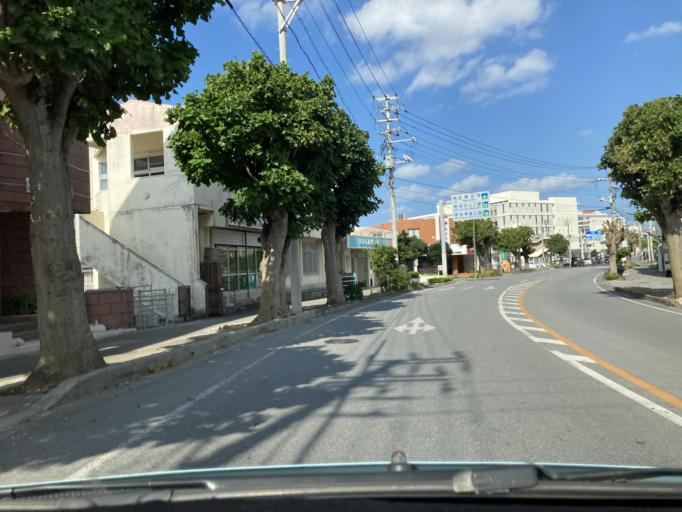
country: JP
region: Okinawa
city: Tomigusuku
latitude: 26.1756
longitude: 127.6830
